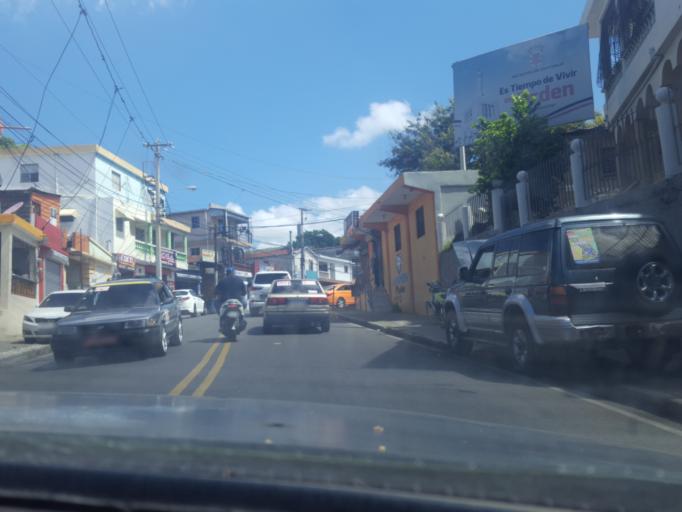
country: DO
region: Santiago
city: Santiago de los Caballeros
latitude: 19.4765
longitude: -70.7105
